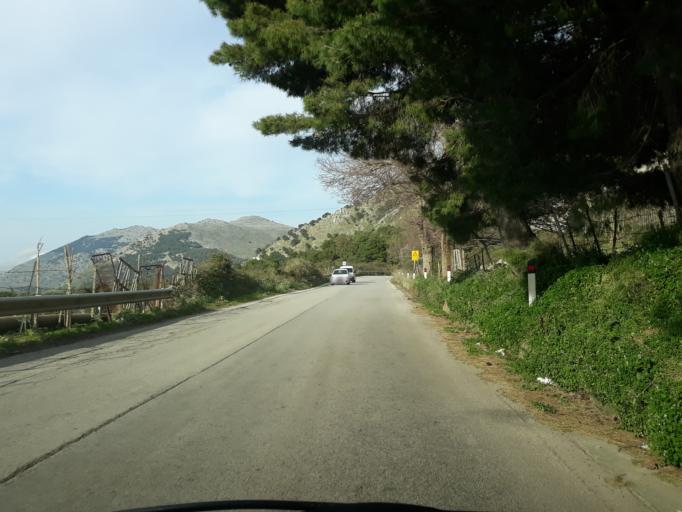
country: IT
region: Sicily
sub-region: Palermo
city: Torretta
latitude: 38.1086
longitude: 13.2360
